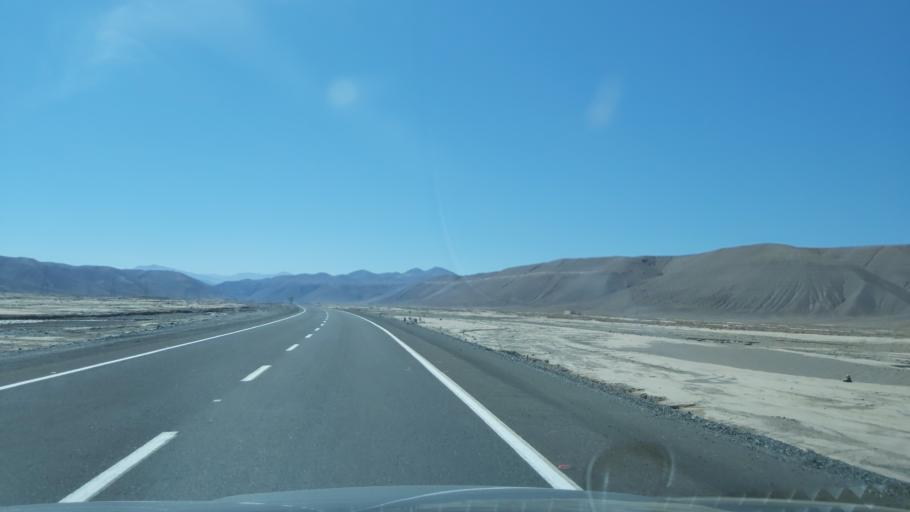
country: CL
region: Atacama
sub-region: Provincia de Chanaral
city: Diego de Almagro
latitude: -26.3535
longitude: -69.9094
